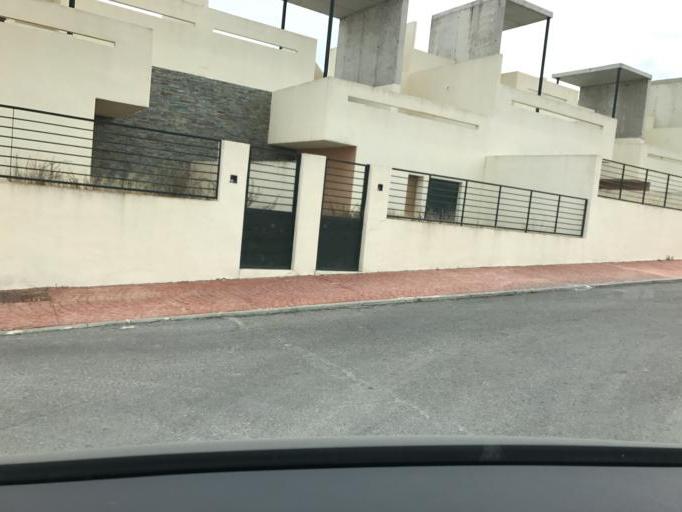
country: ES
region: Andalusia
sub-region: Provincia de Granada
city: Las Gabias
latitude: 37.1249
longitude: -3.6704
